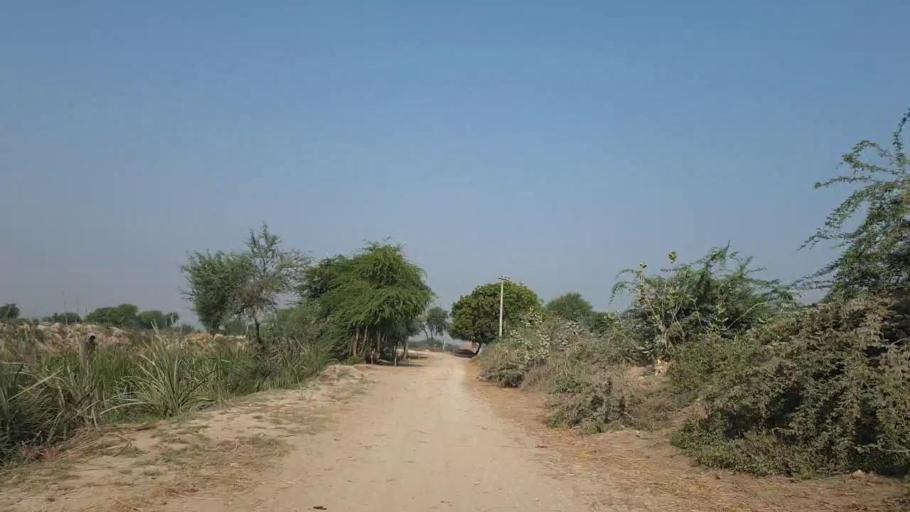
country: PK
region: Sindh
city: Matli
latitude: 24.9884
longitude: 68.6253
